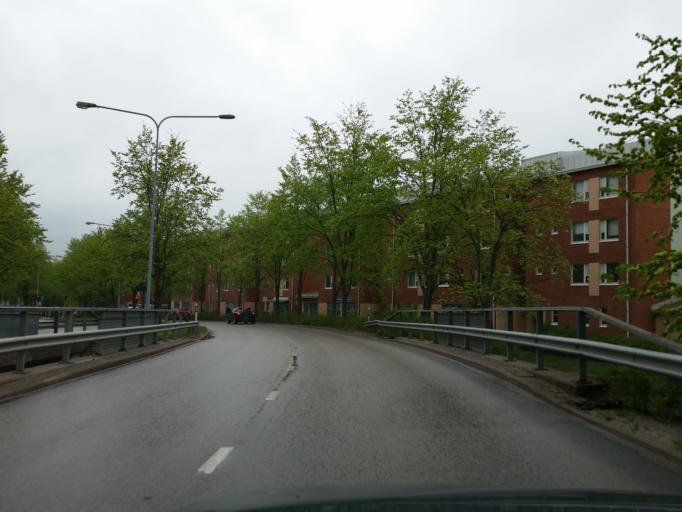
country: FI
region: Uusimaa
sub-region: Helsinki
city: Kilo
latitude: 60.2240
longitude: 24.8104
